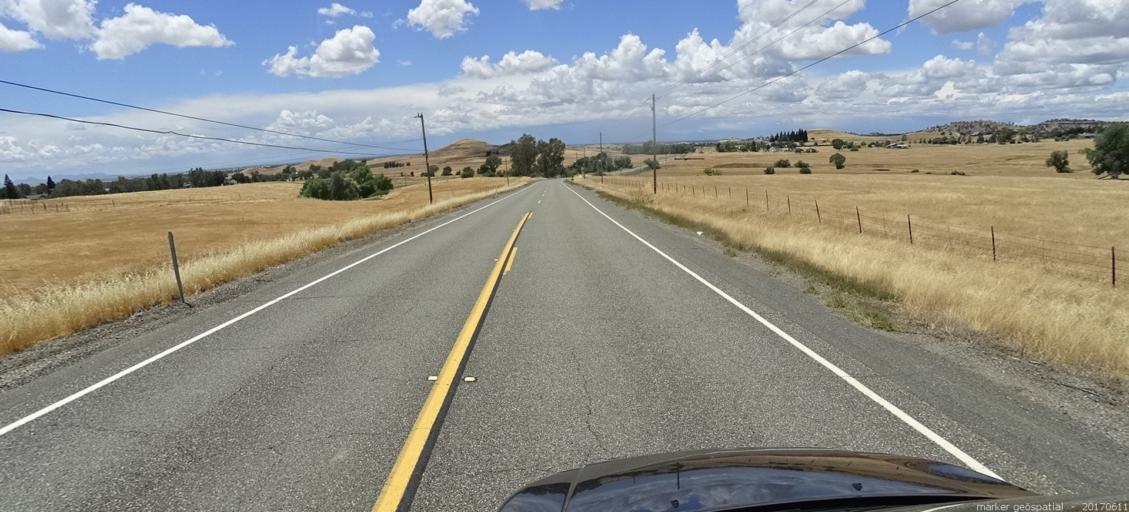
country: US
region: California
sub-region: Butte County
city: Paradise
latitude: 39.6484
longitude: -121.6050
